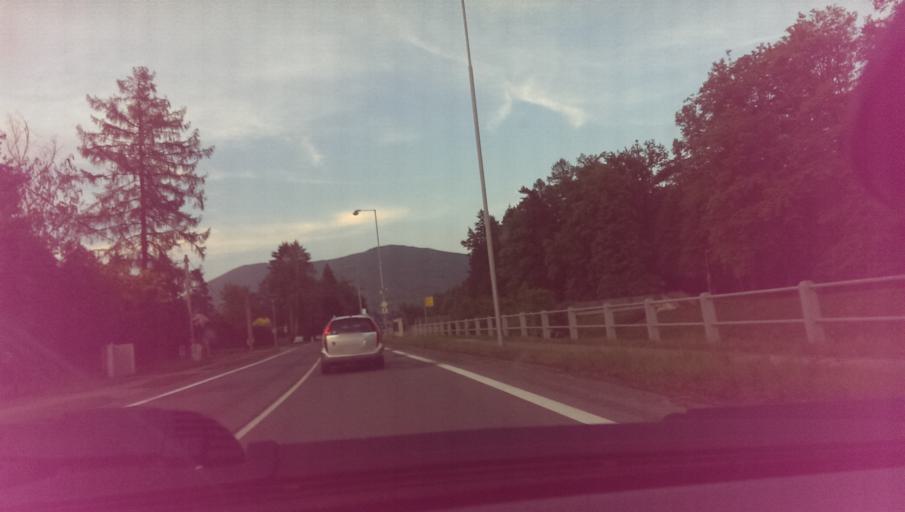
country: CZ
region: Zlin
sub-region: Okres Vsetin
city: Roznov pod Radhostem
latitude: 49.4634
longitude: 18.1479
